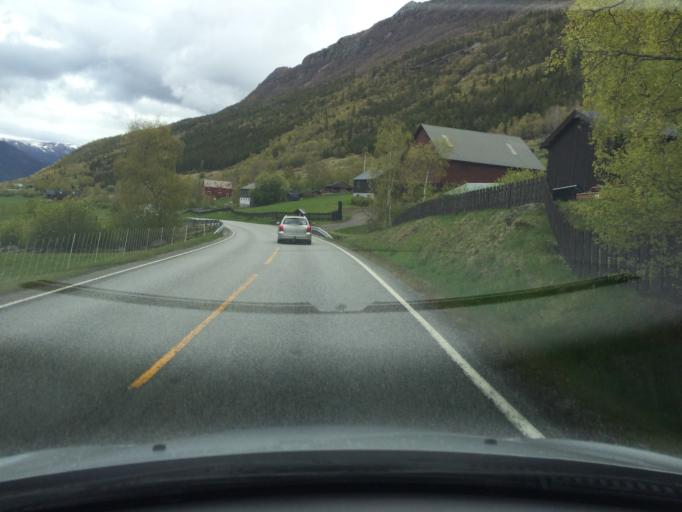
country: NO
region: Oppland
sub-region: Lom
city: Fossbergom
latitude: 61.8188
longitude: 8.5269
